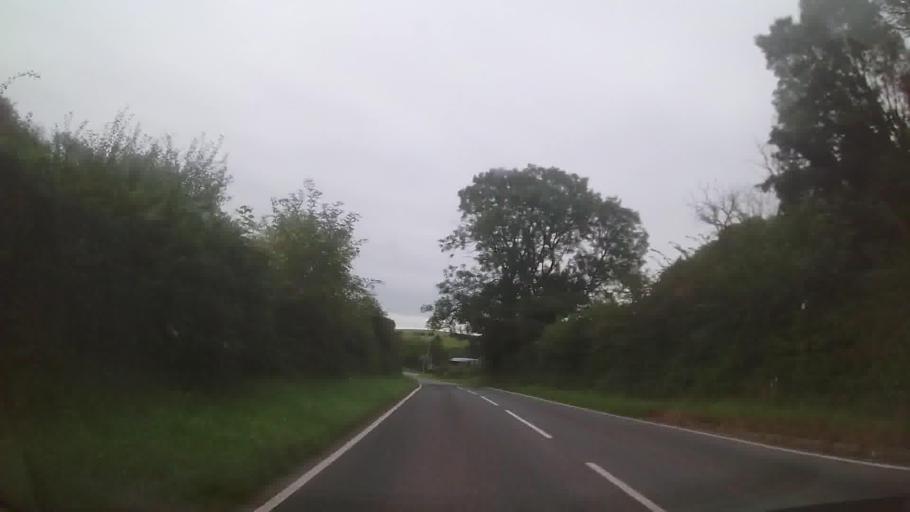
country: GB
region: Wales
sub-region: Carmarthenshire
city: Saint Clears
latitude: 51.7595
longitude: -4.4861
